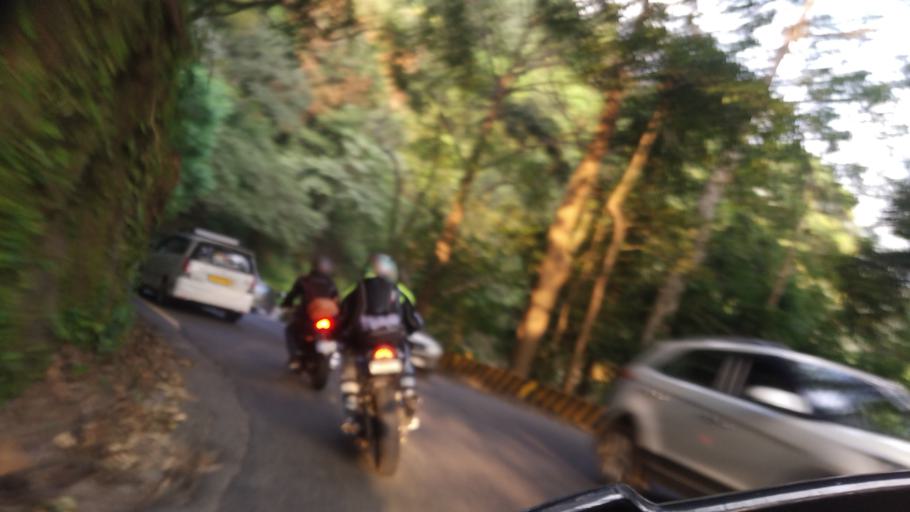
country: IN
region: Kerala
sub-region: Wayanad
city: Kalpetta
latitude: 11.5100
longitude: 76.0239
